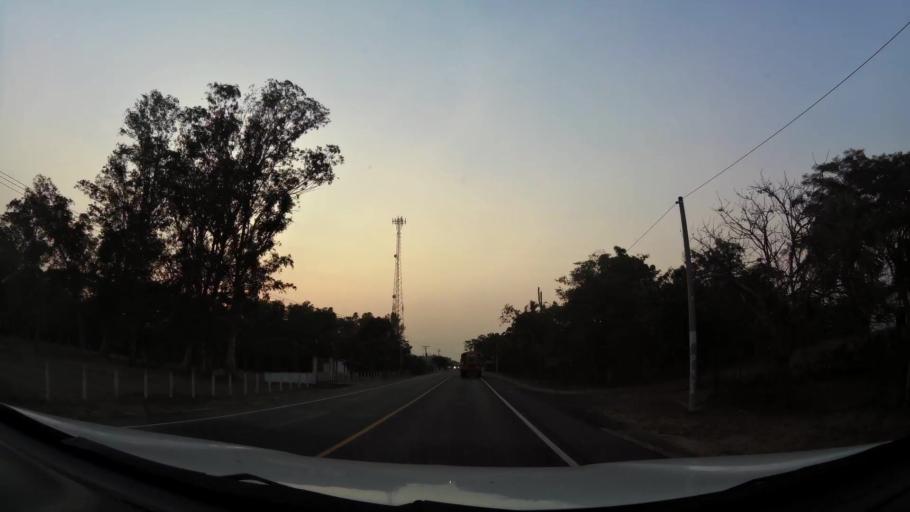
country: NI
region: Leon
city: Leon
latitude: 12.3361
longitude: -86.8118
